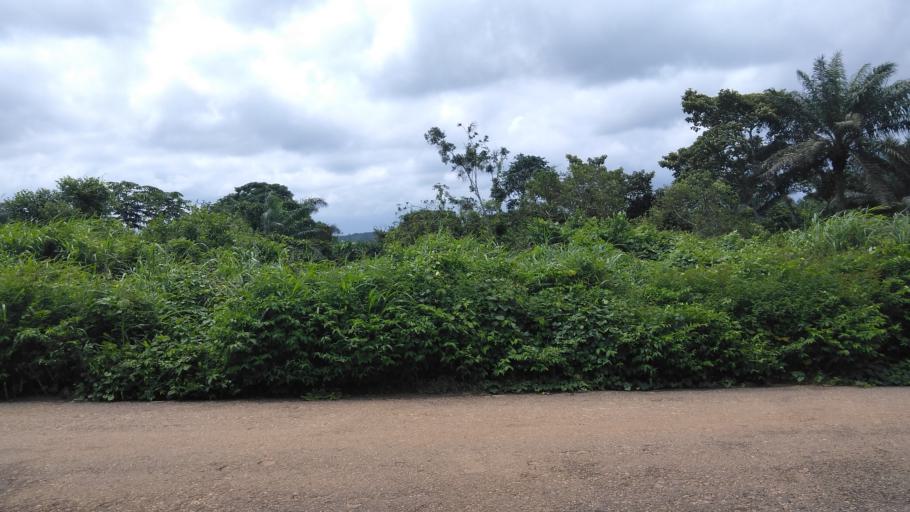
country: NG
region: Ogun
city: Abigi
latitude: 6.6129
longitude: 4.5500
